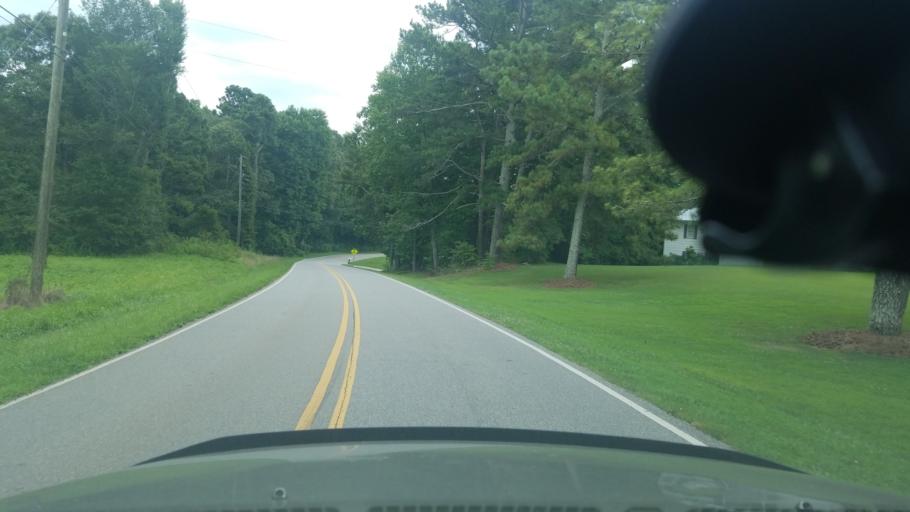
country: US
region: Georgia
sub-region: Forsyth County
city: Cumming
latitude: 34.3148
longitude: -84.1711
